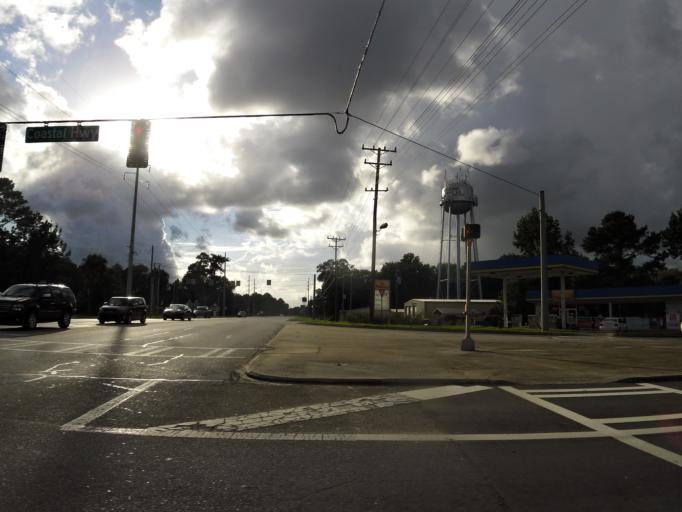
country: US
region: Georgia
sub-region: Liberty County
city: Midway
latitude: 31.7999
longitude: -81.4328
